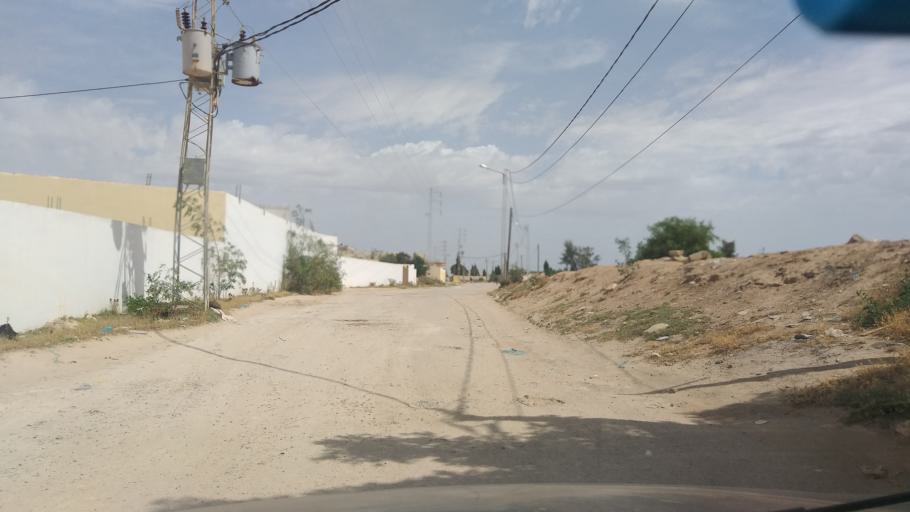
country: TN
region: Al Mahdiyah
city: El Jem
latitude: 35.3070
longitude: 10.7038
